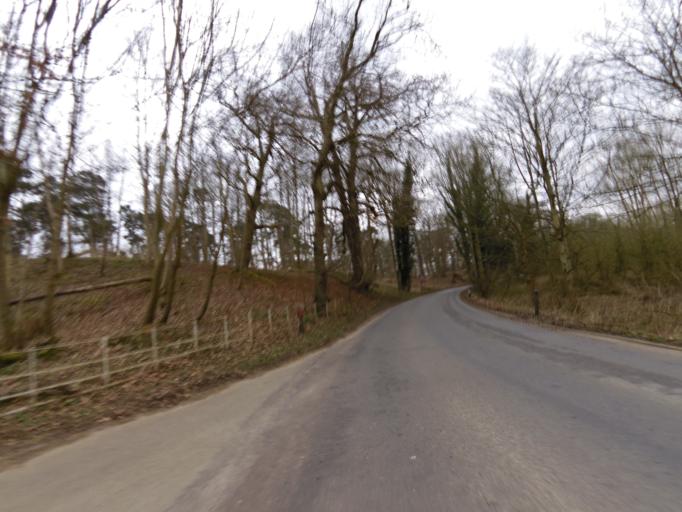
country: GB
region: England
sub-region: Suffolk
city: Wickham Market
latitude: 52.1648
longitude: 1.3576
